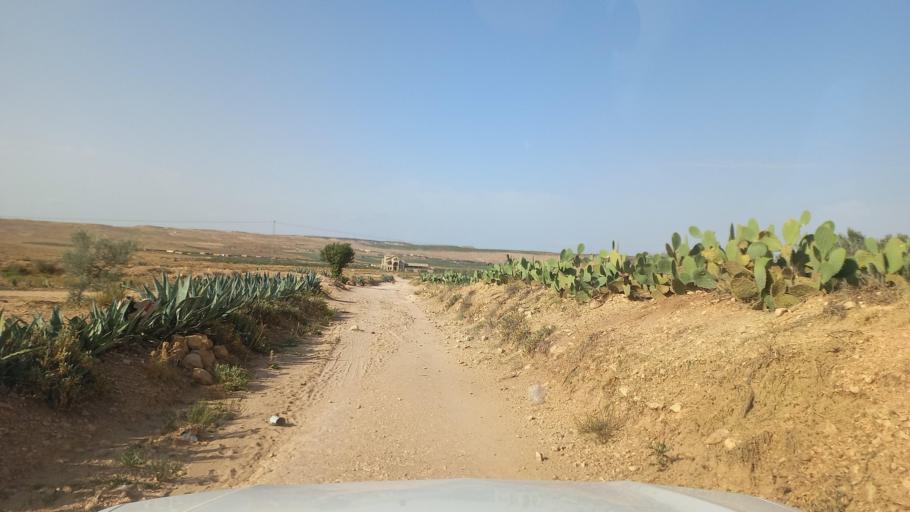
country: TN
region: Al Qasrayn
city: Kasserine
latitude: 35.3391
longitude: 8.8451
